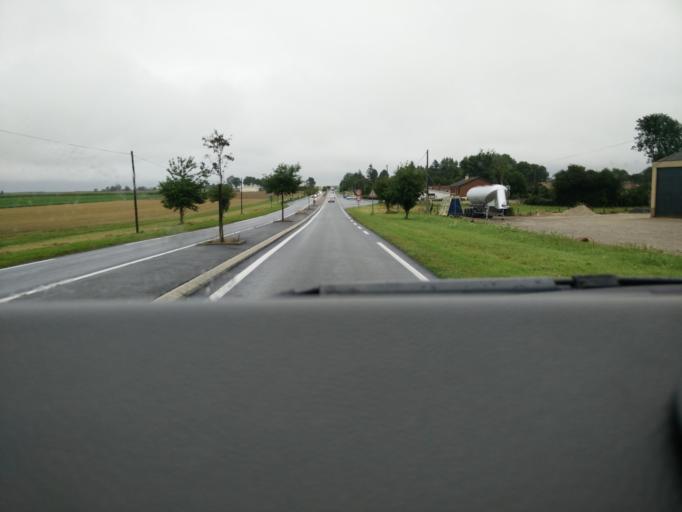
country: FR
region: Nord-Pas-de-Calais
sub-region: Departement du Pas-de-Calais
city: Auchy-les-Hesdin
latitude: 50.3915
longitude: 2.2102
